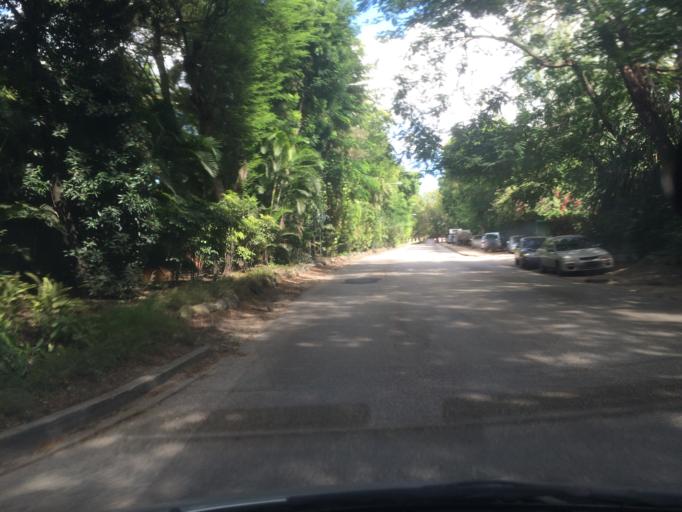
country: BB
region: Saint James
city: Holetown
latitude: 13.1704
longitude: -59.6369
